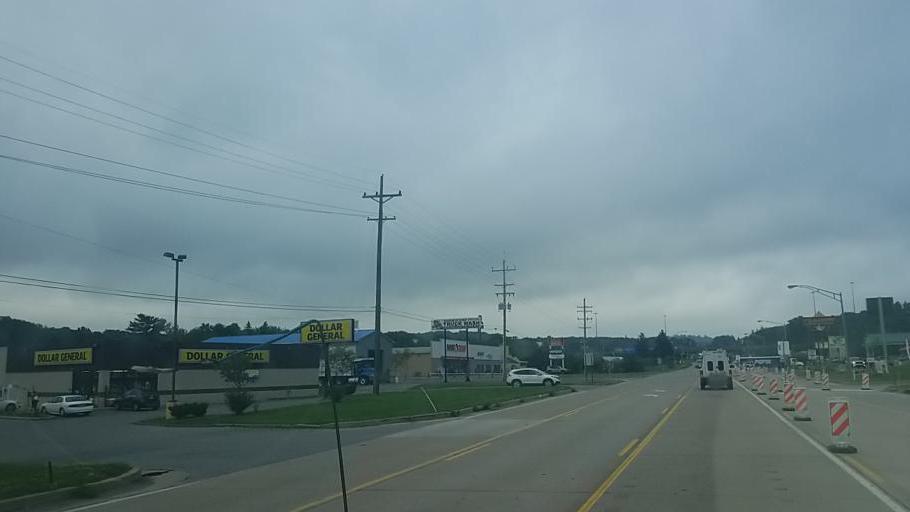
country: US
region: Pennsylvania
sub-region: Jefferson County
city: Brookville
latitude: 41.1658
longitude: -79.0976
